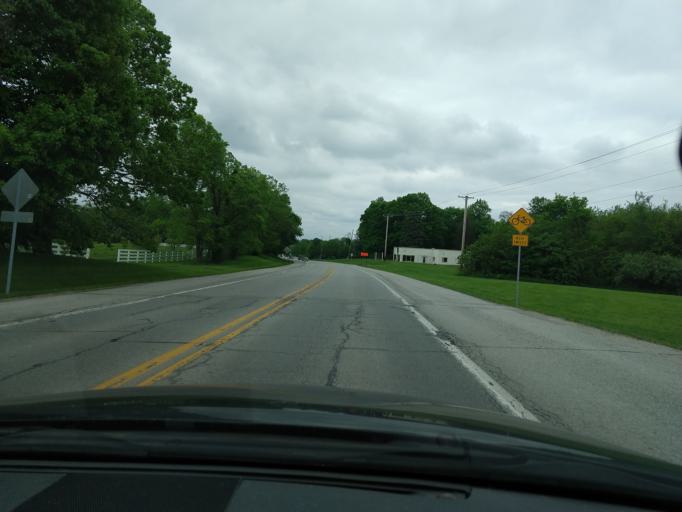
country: US
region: Indiana
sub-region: Hamilton County
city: Noblesville
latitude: 40.0440
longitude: -86.0375
